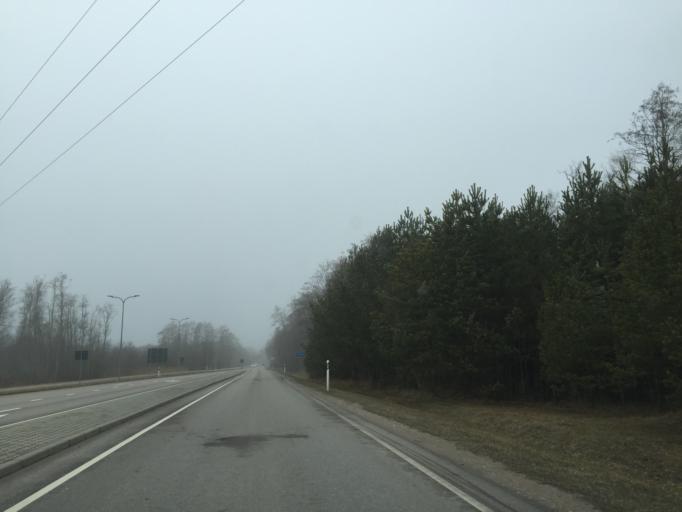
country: EE
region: Saare
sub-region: Kuressaare linn
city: Kuressaare
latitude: 58.2317
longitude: 22.4141
